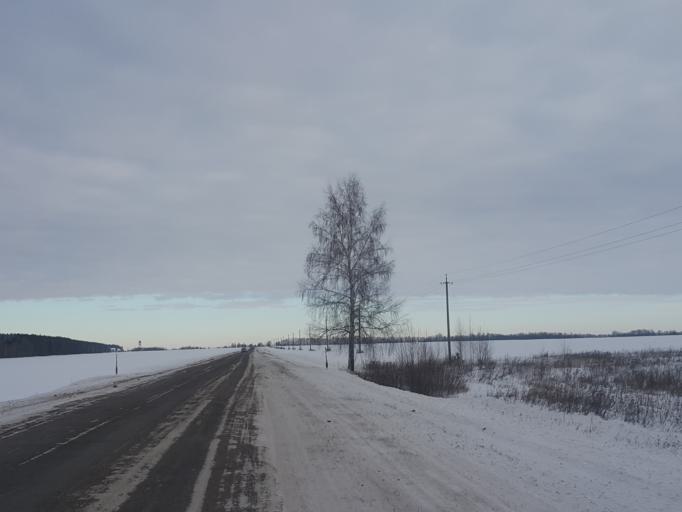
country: RU
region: Tambov
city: Novaya Lyada
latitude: 52.7556
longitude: 41.7222
